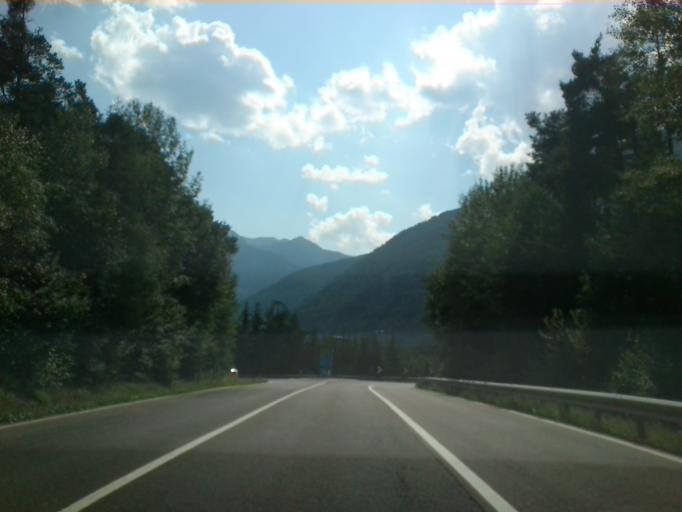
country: IT
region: Trentino-Alto Adige
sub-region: Bolzano
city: Naz-Sciaves - Natz-Schabs
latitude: 46.7663
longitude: 11.6451
